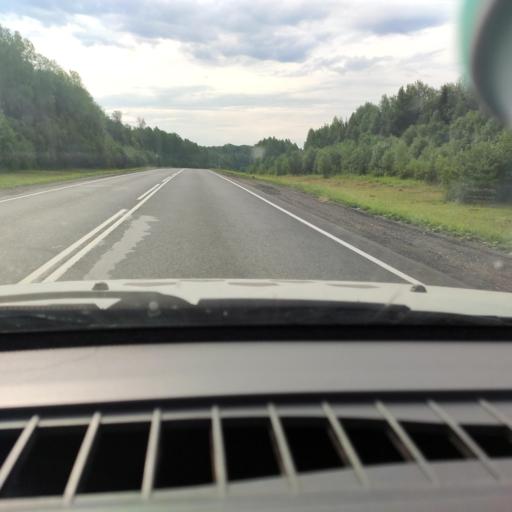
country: RU
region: Kirov
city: Kostino
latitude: 58.7293
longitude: 53.6498
